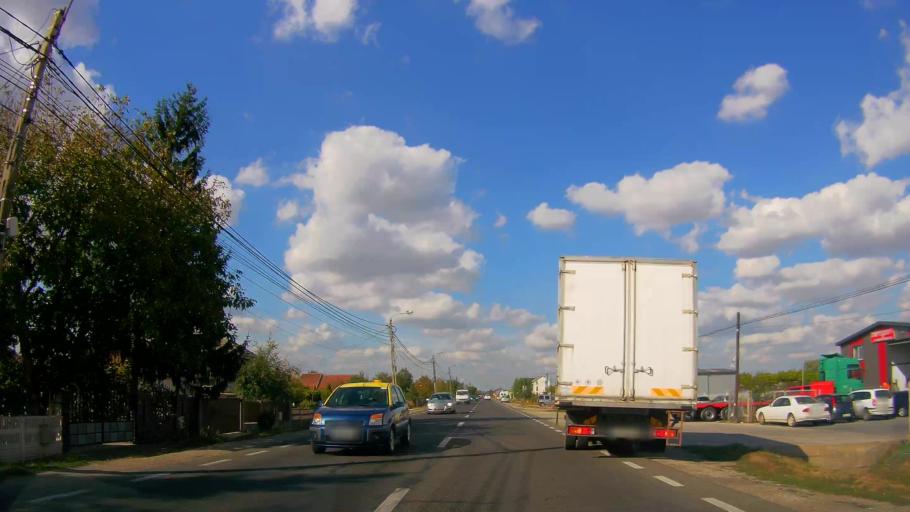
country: RO
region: Satu Mare
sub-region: Comuna Paulesti
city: Paulesti
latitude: 47.7525
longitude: 22.8831
